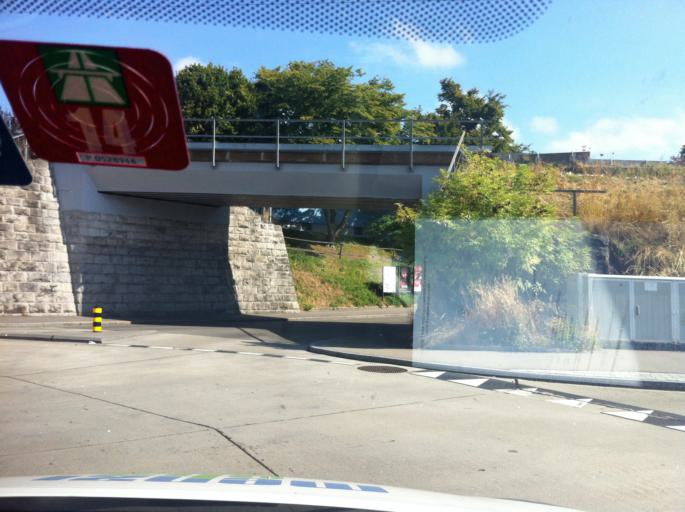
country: CH
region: Zurich
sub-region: Bezirk Buelach
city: Buelach / Seematt
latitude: 47.5206
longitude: 8.5465
